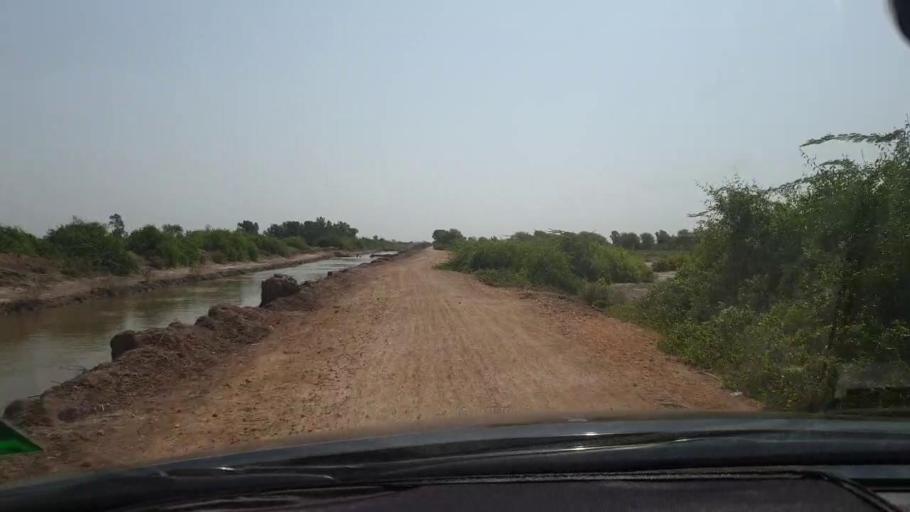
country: PK
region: Sindh
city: Tando Bago
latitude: 24.7961
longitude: 69.1076
